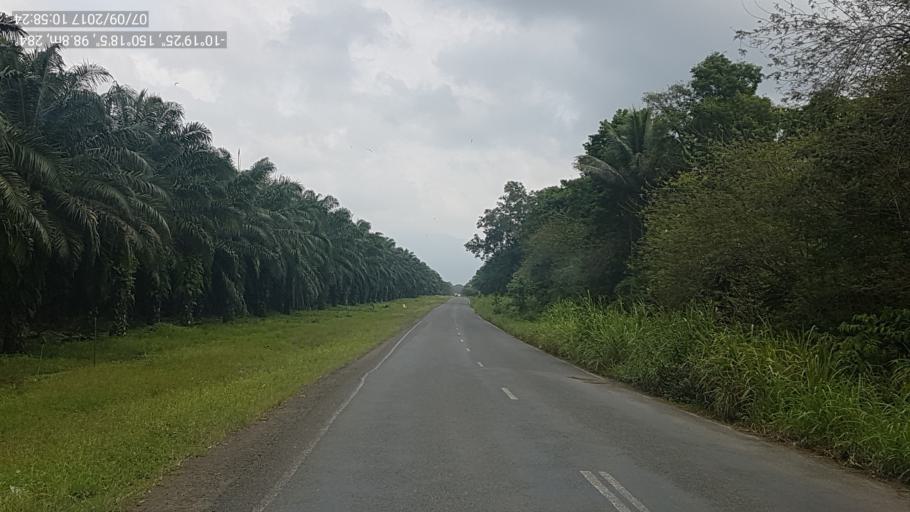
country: PG
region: Milne Bay
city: Alotau
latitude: -10.3239
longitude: 150.3017
